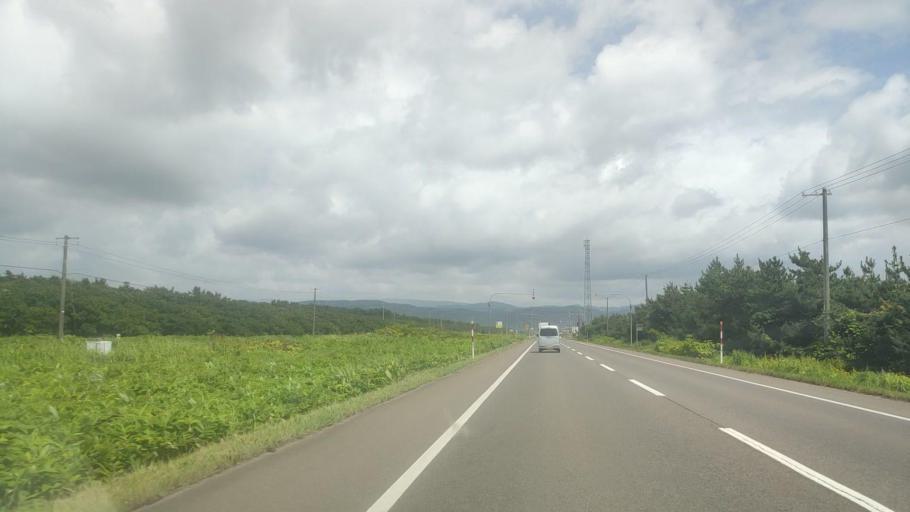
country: JP
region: Hokkaido
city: Niseko Town
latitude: 42.5519
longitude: 140.4197
